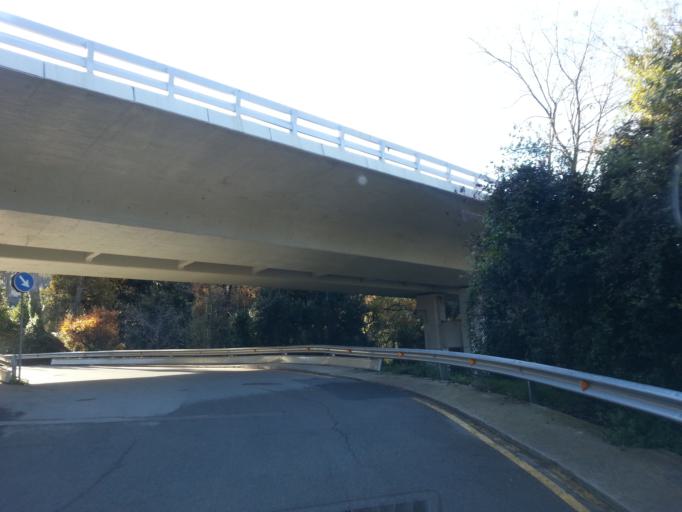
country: ES
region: Catalonia
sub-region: Provincia de Barcelona
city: Sant Cugat del Valles
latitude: 41.4277
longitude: 2.0898
